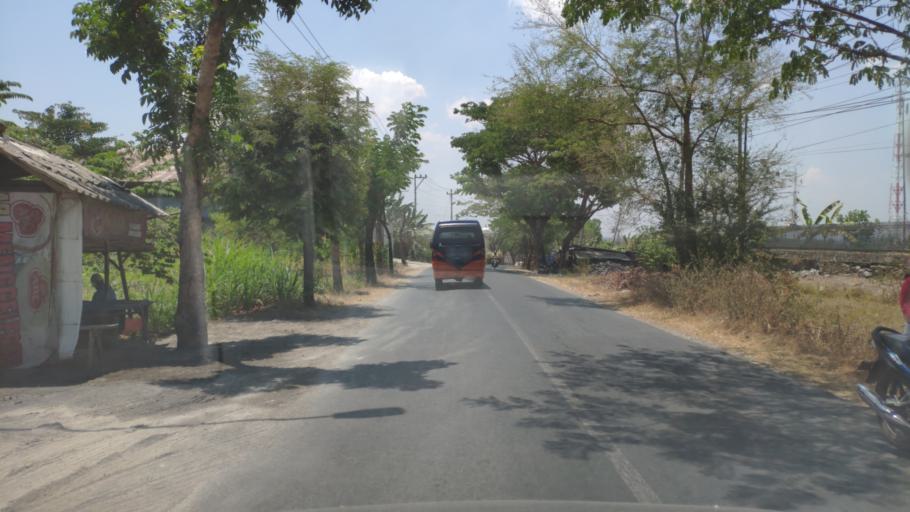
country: ID
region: Central Java
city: Tambakkromo
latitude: -7.1488
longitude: 111.5773
